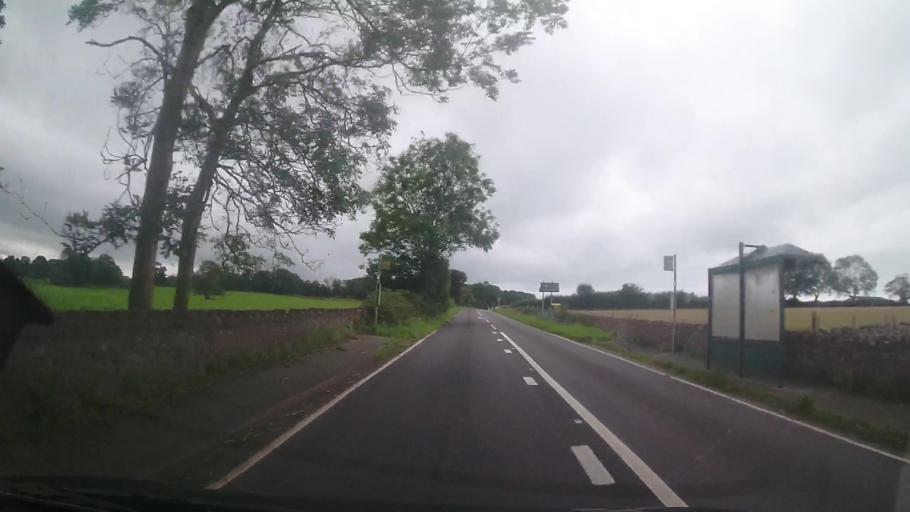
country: GB
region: Wales
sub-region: Gwynedd
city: Y Felinheli
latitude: 53.1981
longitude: -4.2322
